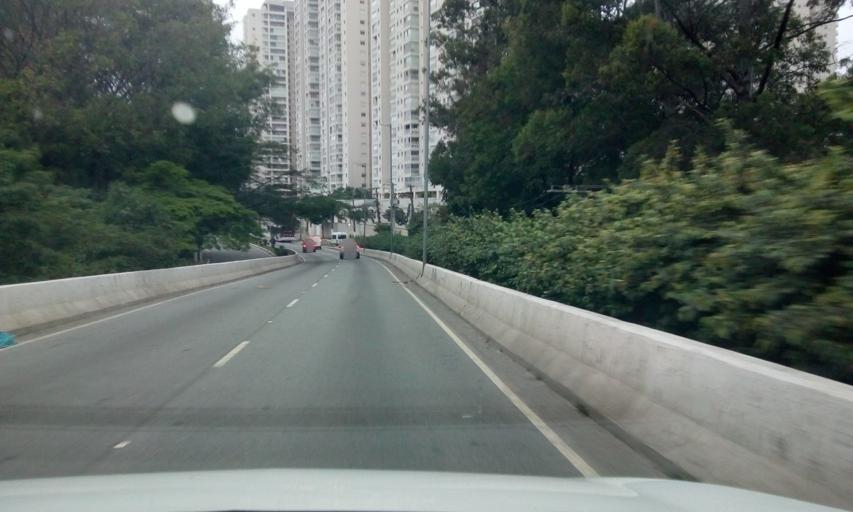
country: BR
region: Sao Paulo
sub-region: Taboao Da Serra
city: Taboao da Serra
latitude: -23.6520
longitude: -46.7217
